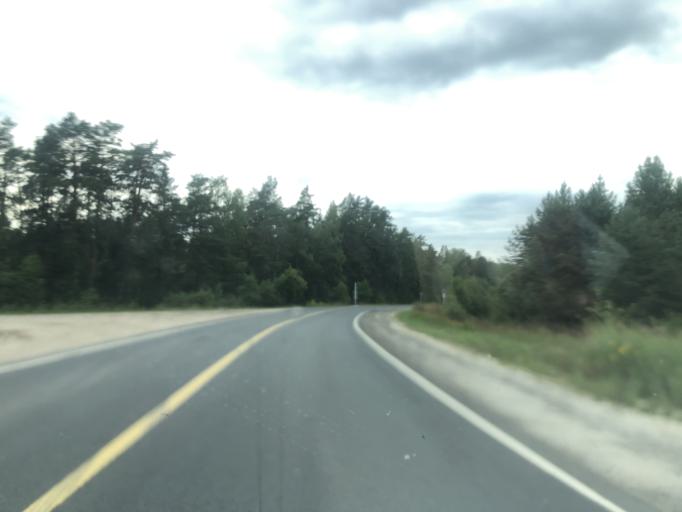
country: RU
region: Ivanovo
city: Pestyaki
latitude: 56.7012
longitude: 42.7116
